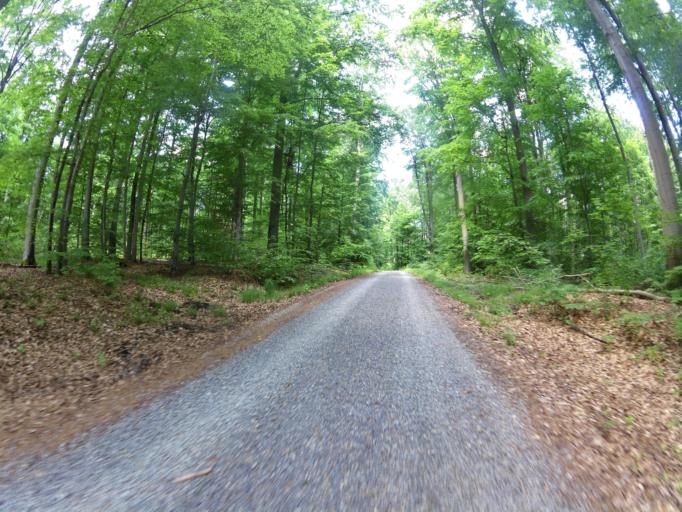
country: DE
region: Bavaria
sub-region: Regierungsbezirk Unterfranken
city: Uettingen
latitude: 49.7668
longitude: 9.7618
